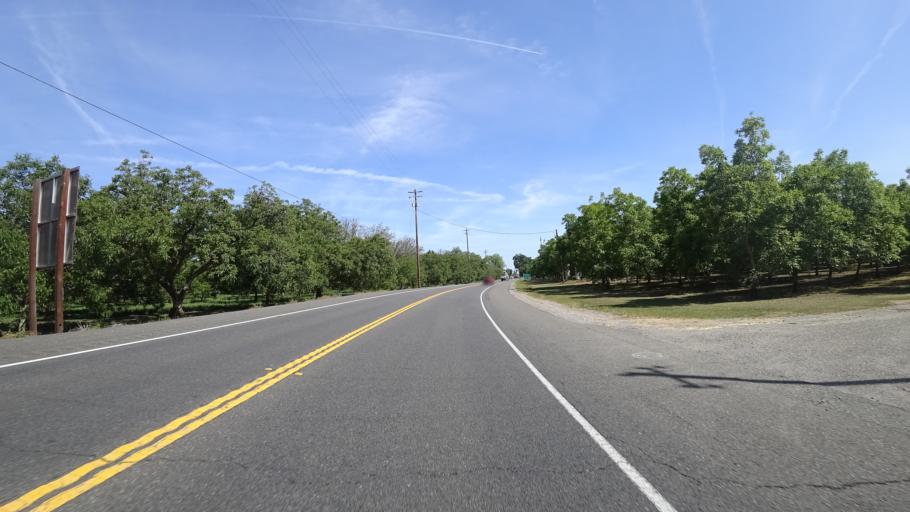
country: US
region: California
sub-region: Tehama County
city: Red Bluff
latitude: 40.1670
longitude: -122.1564
